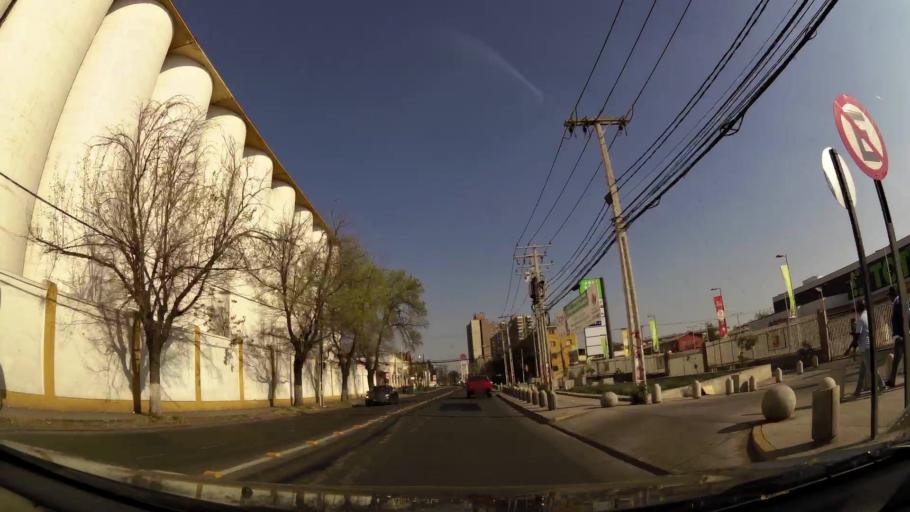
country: CL
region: Santiago Metropolitan
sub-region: Provincia de Santiago
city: Santiago
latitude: -33.4186
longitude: -70.6635
